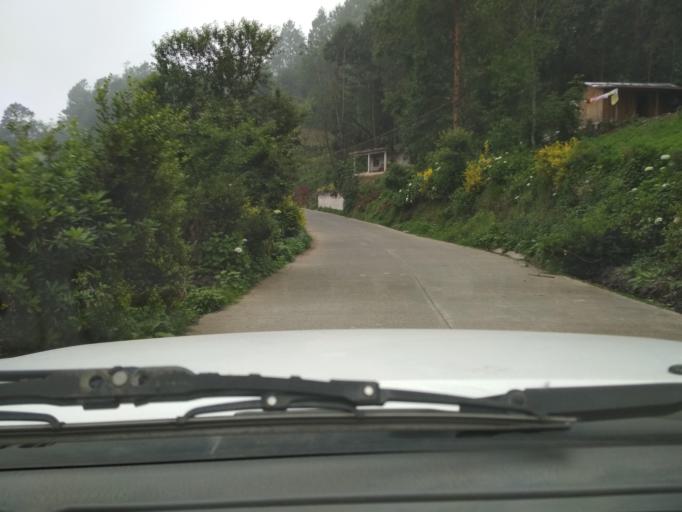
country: MX
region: Veracruz
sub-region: La Perla
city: Chilapa
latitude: 18.9747
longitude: -97.1662
